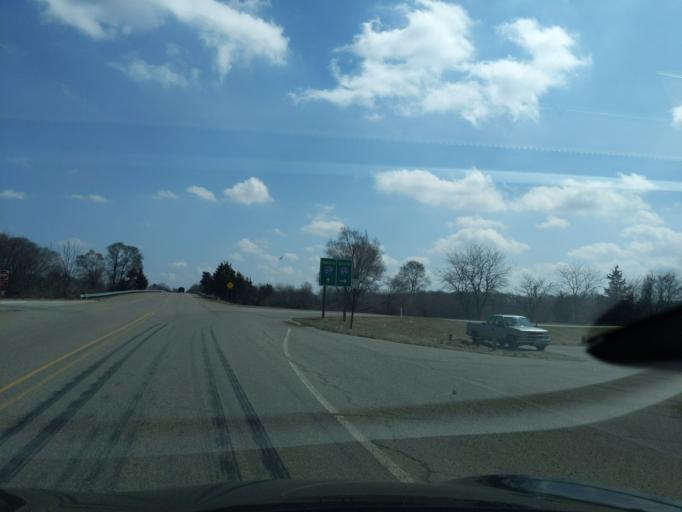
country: US
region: Michigan
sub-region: Calhoun County
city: Marshall
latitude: 42.3499
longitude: -84.9848
